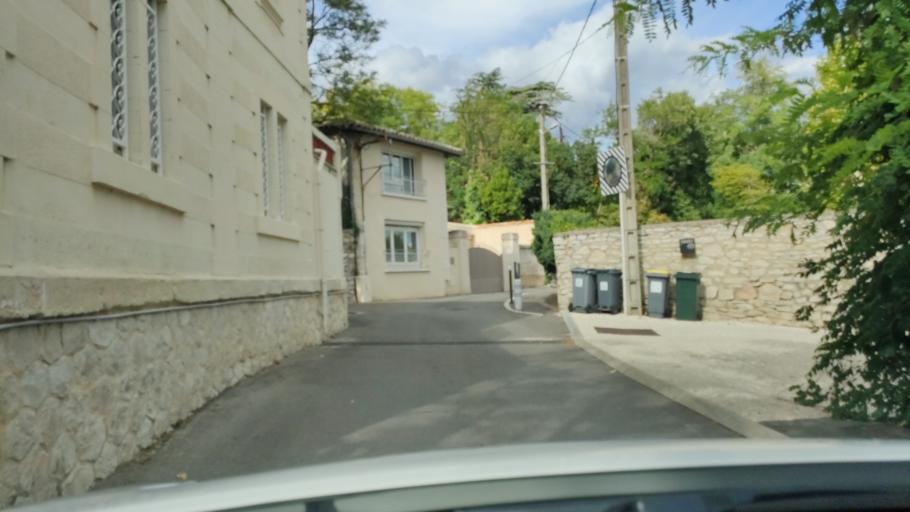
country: FR
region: Languedoc-Roussillon
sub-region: Departement du Gard
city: Villeneuve-les-Avignon
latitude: 43.9583
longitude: 4.7907
